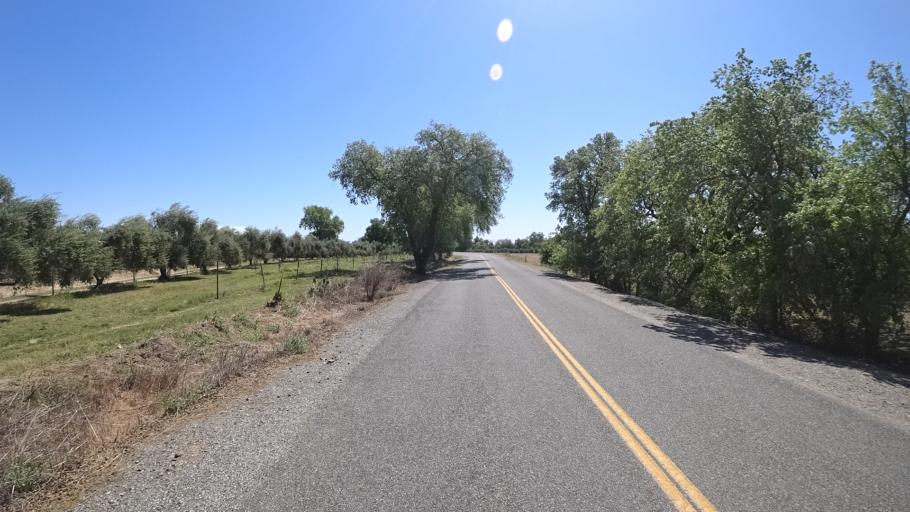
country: US
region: California
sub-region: Glenn County
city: Orland
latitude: 39.7855
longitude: -122.2179
